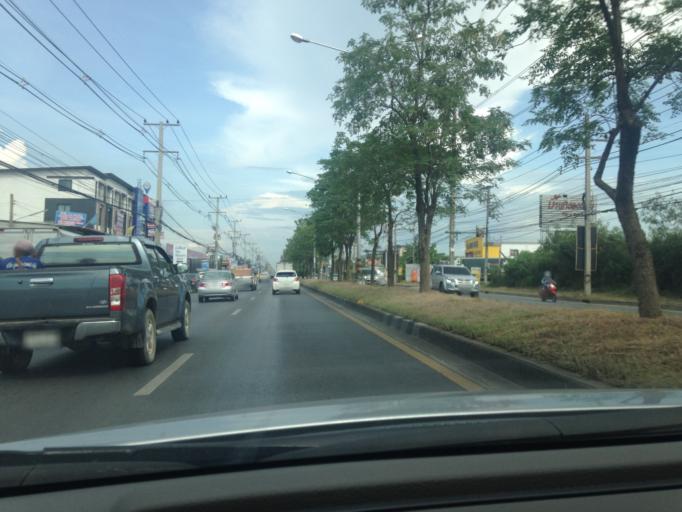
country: TH
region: Pathum Thani
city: Khlong Luang
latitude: 14.0661
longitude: 100.6676
